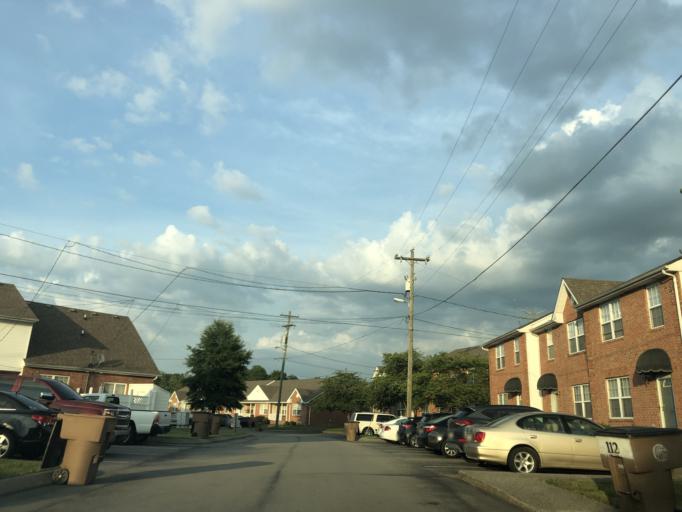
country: US
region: Tennessee
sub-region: Davidson County
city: Nashville
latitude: 36.1634
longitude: -86.7026
